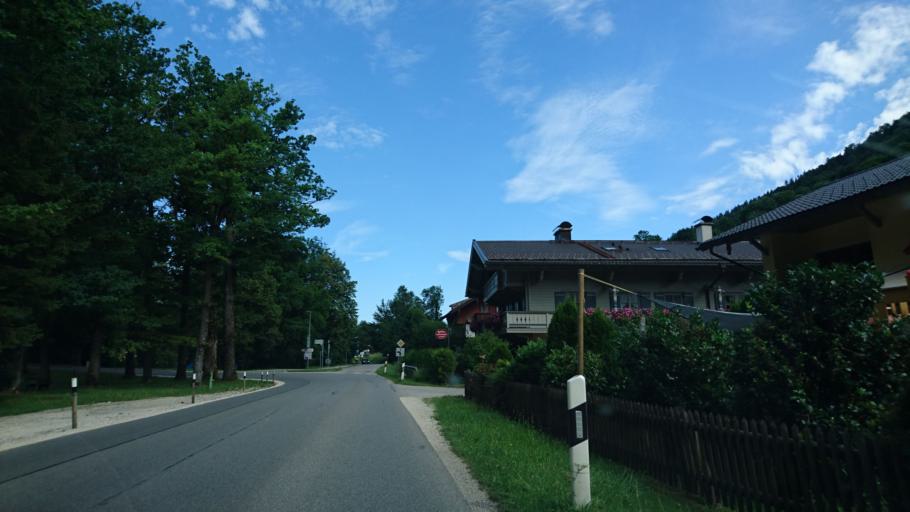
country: DE
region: Bavaria
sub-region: Upper Bavaria
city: Ruhpolding
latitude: 47.7609
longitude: 12.6574
